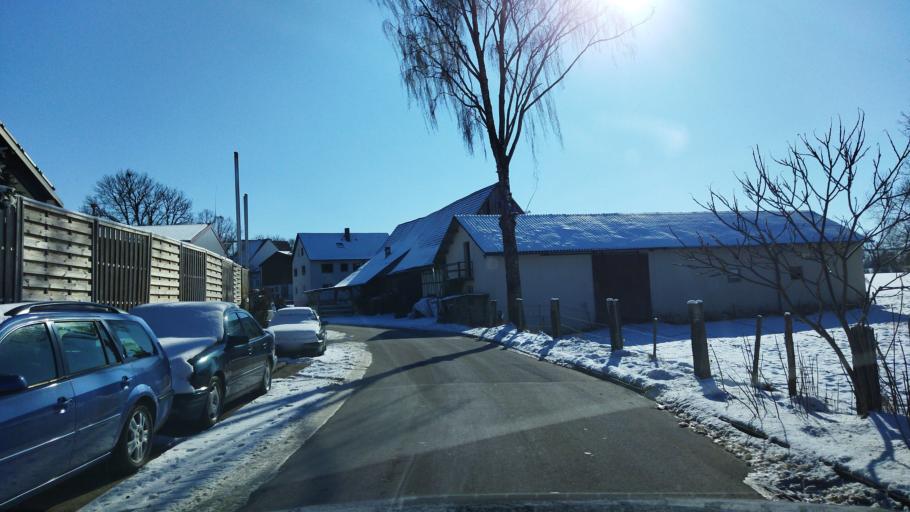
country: DE
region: Baden-Wuerttemberg
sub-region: Regierungsbezirk Stuttgart
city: Ilshofen
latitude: 49.1989
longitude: 9.9349
